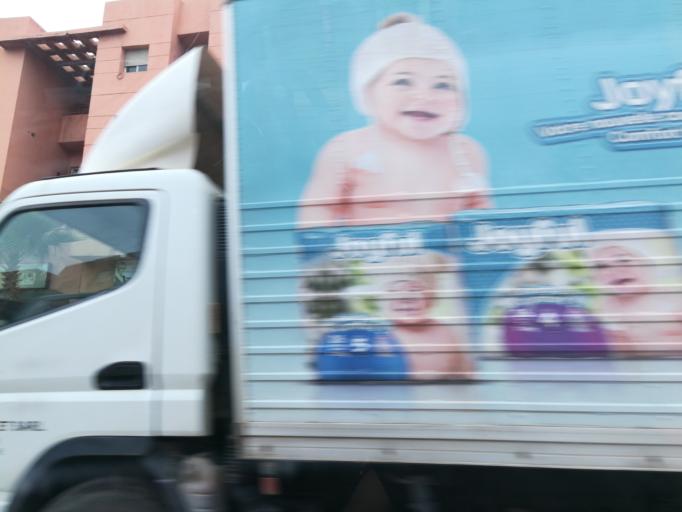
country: MA
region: Marrakech-Tensift-Al Haouz
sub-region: Marrakech
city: Marrakesh
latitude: 31.5759
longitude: -8.0591
